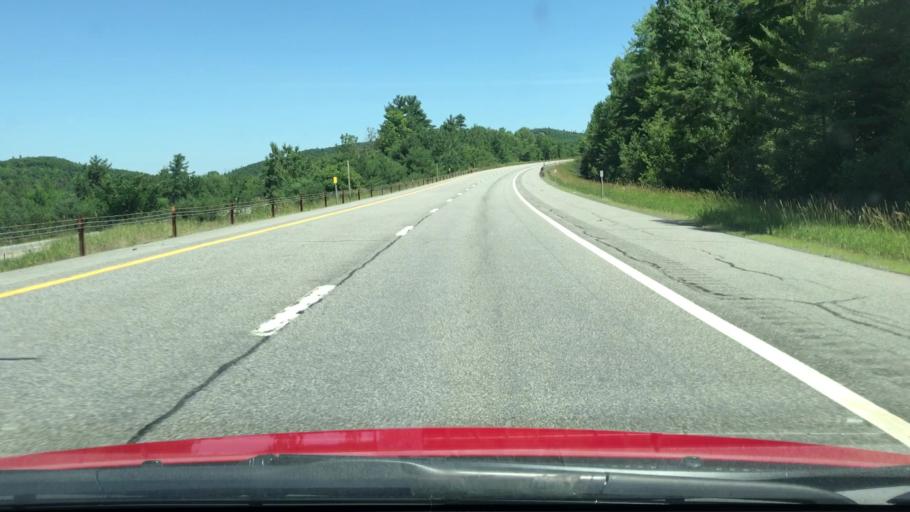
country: US
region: New York
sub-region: Essex County
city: Elizabethtown
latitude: 44.1748
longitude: -73.5814
